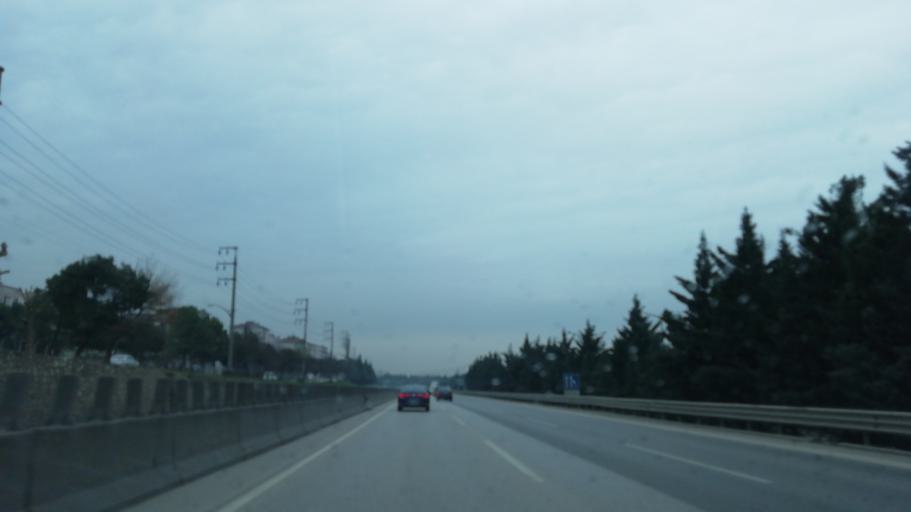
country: TR
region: Kocaeli
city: Derince
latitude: 40.7617
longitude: 29.8649
